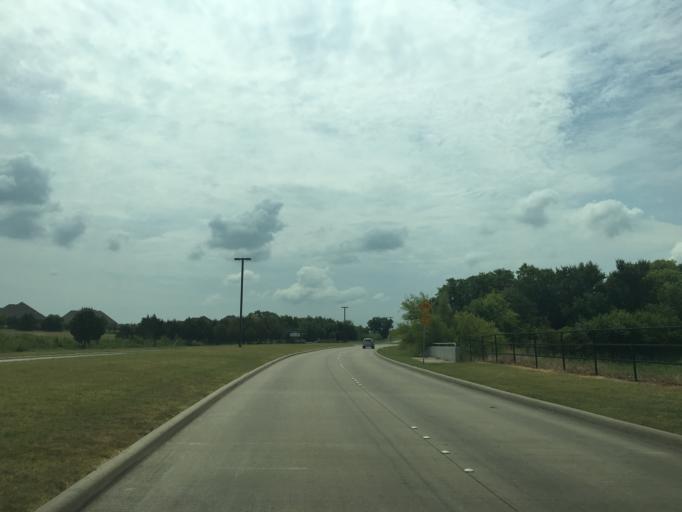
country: US
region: Texas
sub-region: Rockwall County
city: Rockwall
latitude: 32.9788
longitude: -96.4608
